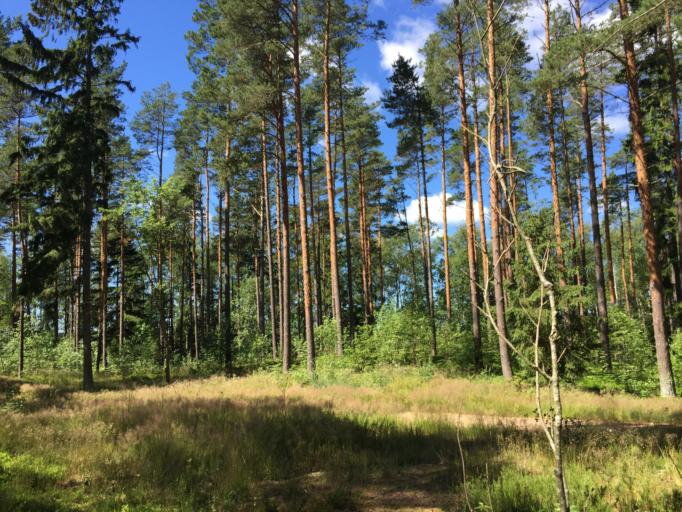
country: LV
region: Ventspils
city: Ventspils
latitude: 57.4405
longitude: 21.6578
